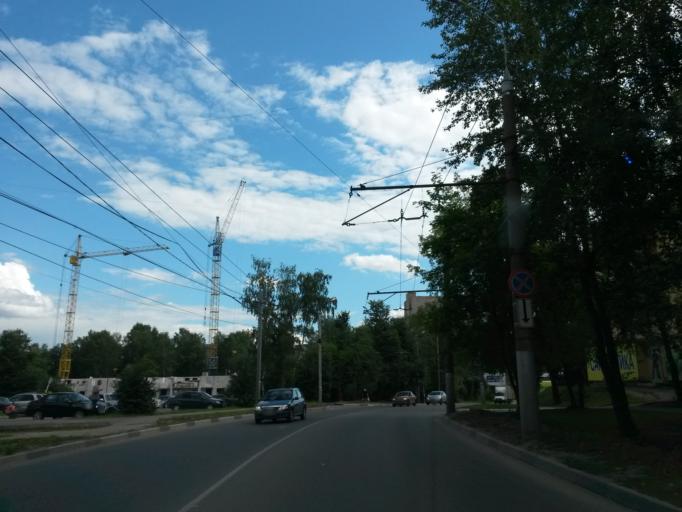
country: RU
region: Ivanovo
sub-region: Gorod Ivanovo
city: Ivanovo
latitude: 56.9851
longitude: 40.9931
